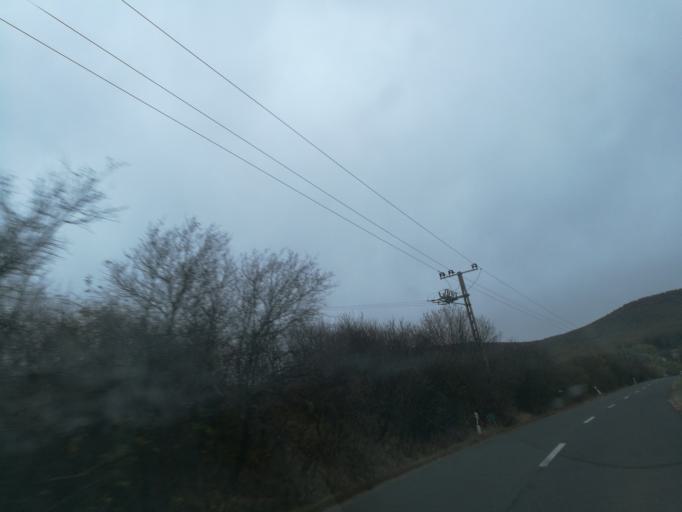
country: HU
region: Nograd
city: Rimoc
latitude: 48.0024
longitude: 19.6169
